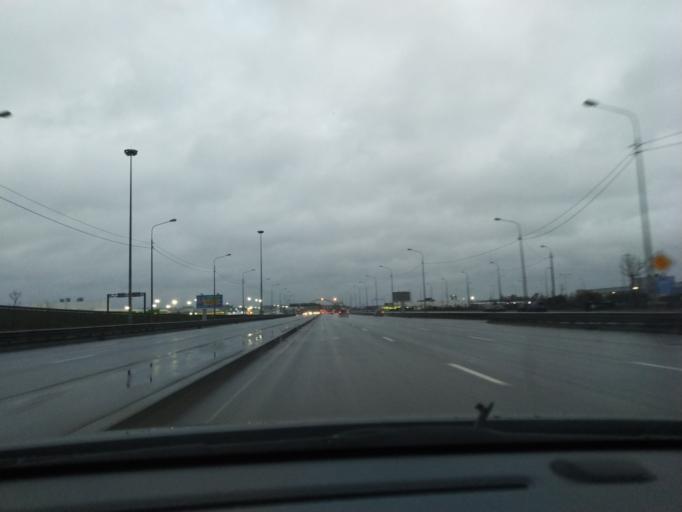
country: RU
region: St.-Petersburg
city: Sosnovaya Polyana
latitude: 59.8021
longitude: 30.1594
